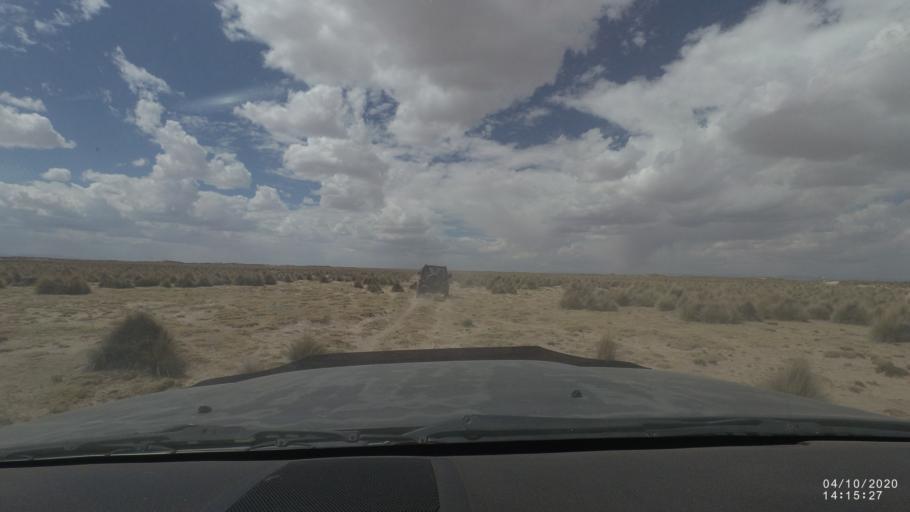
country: BO
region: Oruro
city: Poopo
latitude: -18.6930
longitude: -67.4538
